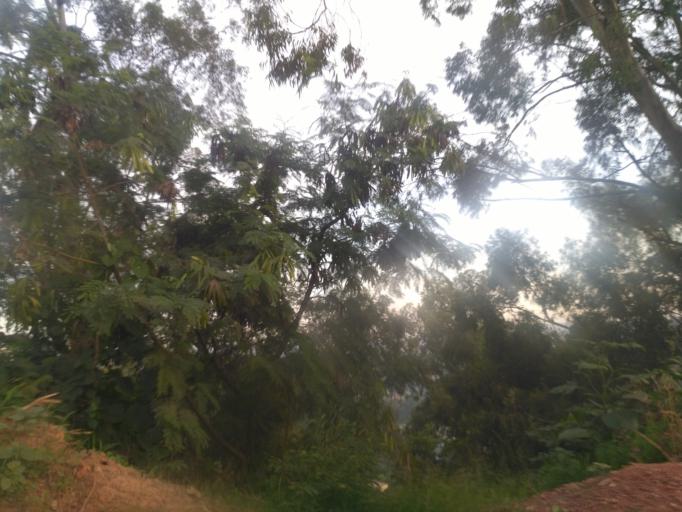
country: UG
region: Central Region
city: Kampala Central Division
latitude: 0.3401
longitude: 32.5796
